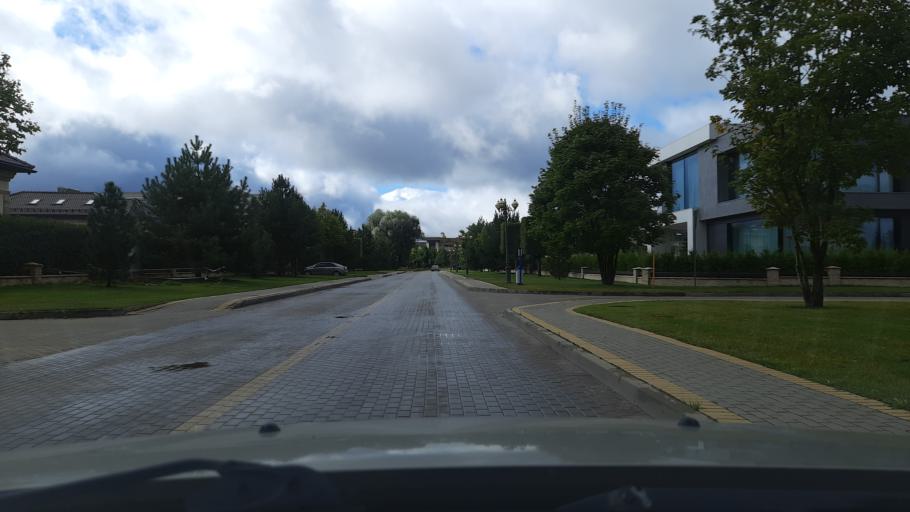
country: RU
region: Moskovskaya
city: Nikolina Gora
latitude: 55.7763
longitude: 37.0527
